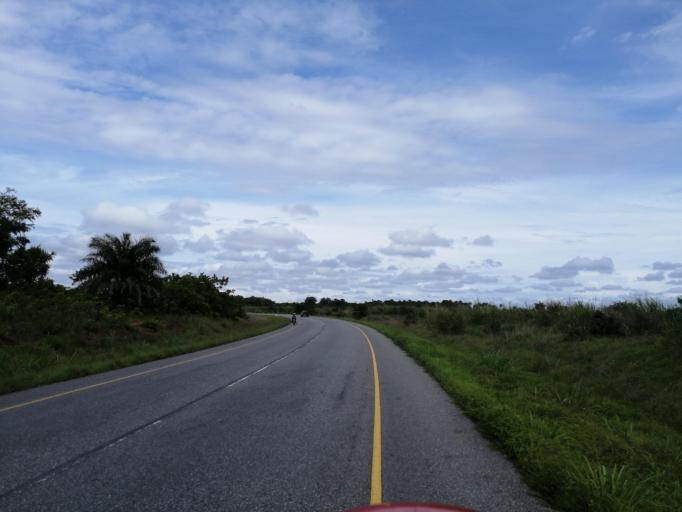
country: SL
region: Northern Province
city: Port Loko
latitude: 8.7354
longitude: -12.9482
